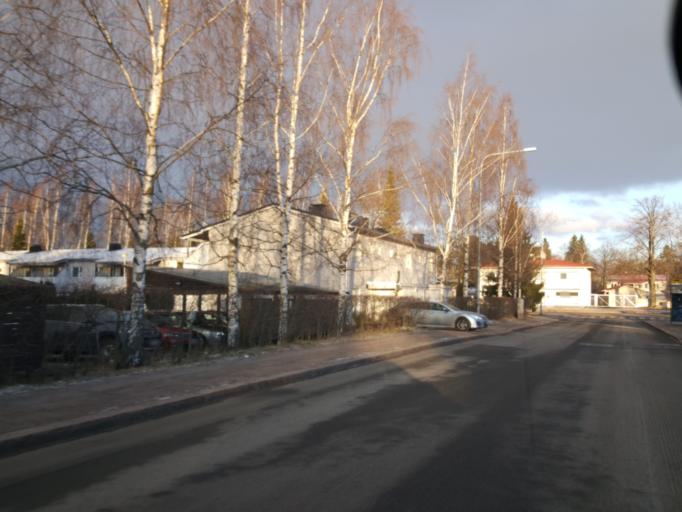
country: FI
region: Uusimaa
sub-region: Helsinki
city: Vantaa
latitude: 60.2508
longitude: 24.9869
